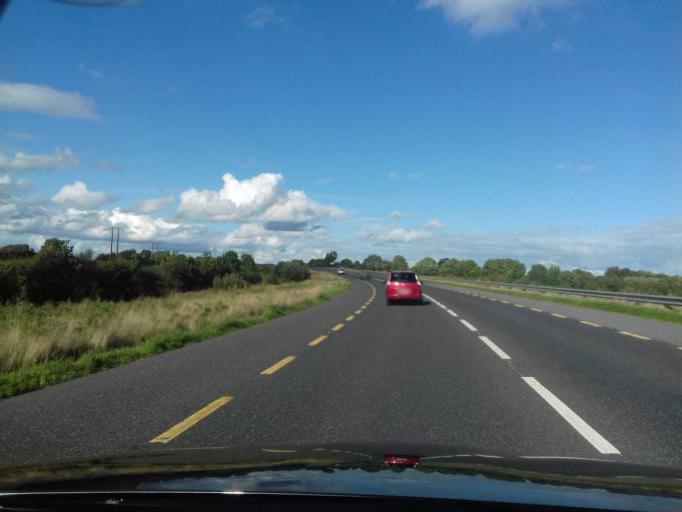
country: IE
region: Leinster
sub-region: Uibh Fhaili
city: Tullamore
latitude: 53.2583
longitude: -7.4684
